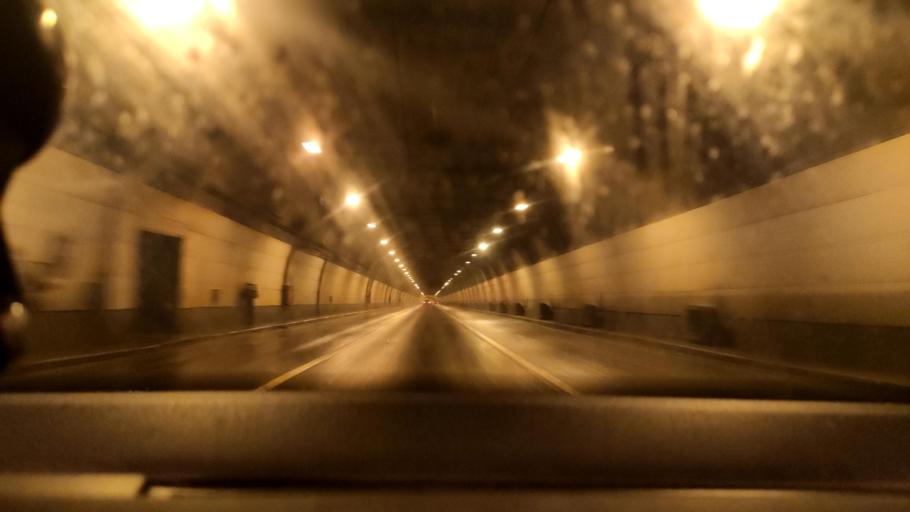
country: RU
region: Moscow
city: Rublevo
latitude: 55.7820
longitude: 37.3934
